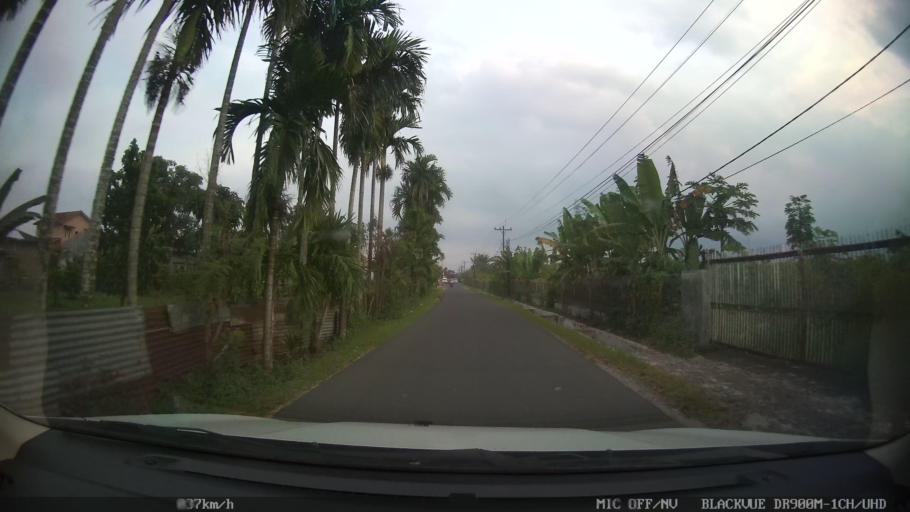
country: ID
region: North Sumatra
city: Sunggal
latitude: 3.5747
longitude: 98.6047
